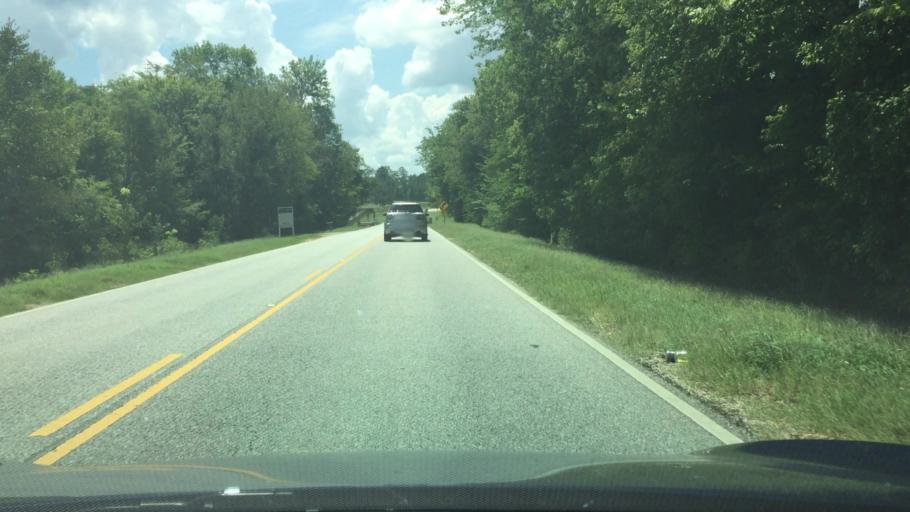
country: US
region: Alabama
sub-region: Montgomery County
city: Pike Road
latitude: 32.2199
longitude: -86.0905
